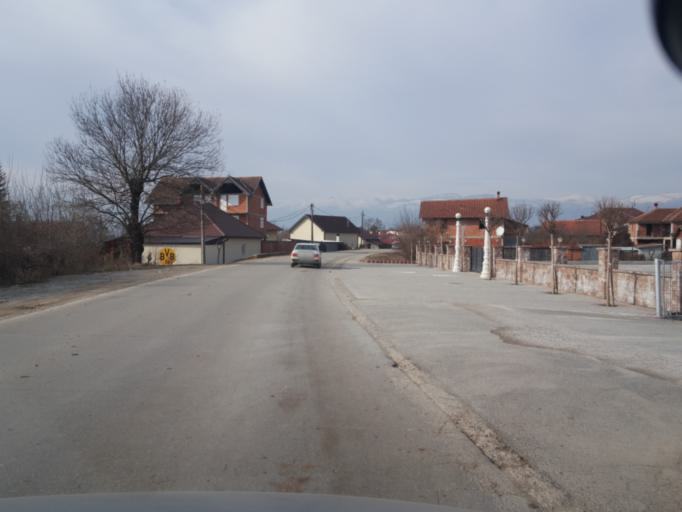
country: XK
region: Pec
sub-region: Komuna e Klines
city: Klina
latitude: 42.6603
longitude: 20.5407
